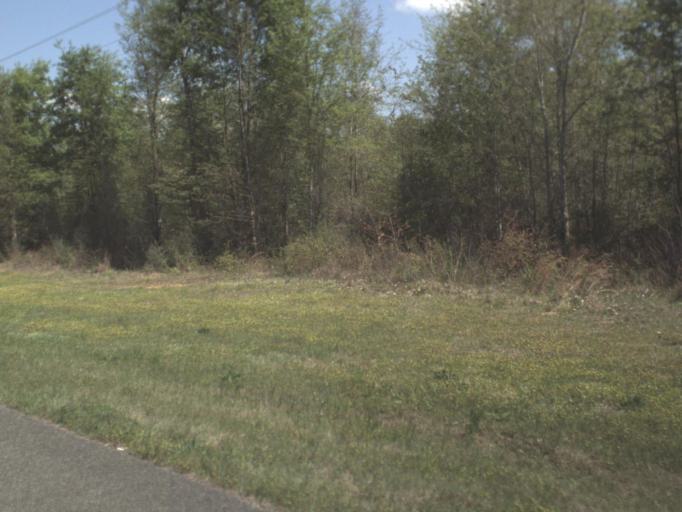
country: US
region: Alabama
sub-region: Escambia County
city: East Brewton
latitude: 30.9265
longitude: -87.0531
